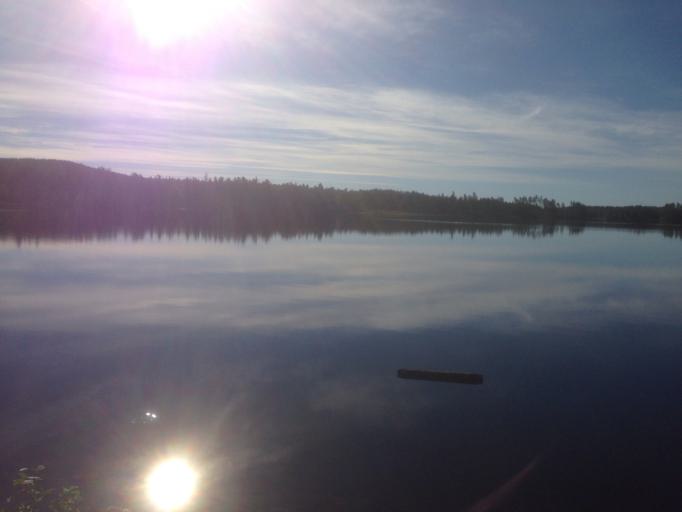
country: SE
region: Dalarna
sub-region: Orsa Kommun
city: Orsa
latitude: 61.5992
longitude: 14.8240
